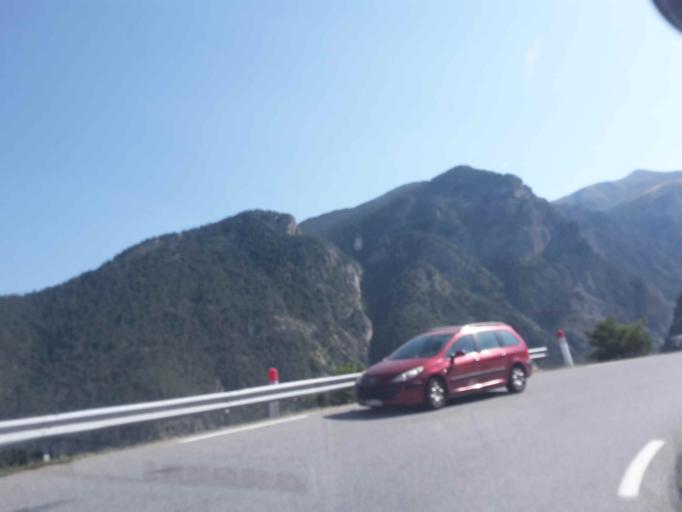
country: FR
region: Provence-Alpes-Cote d'Azur
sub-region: Departement des Hautes-Alpes
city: Guillestre
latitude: 44.6376
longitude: 6.6694
